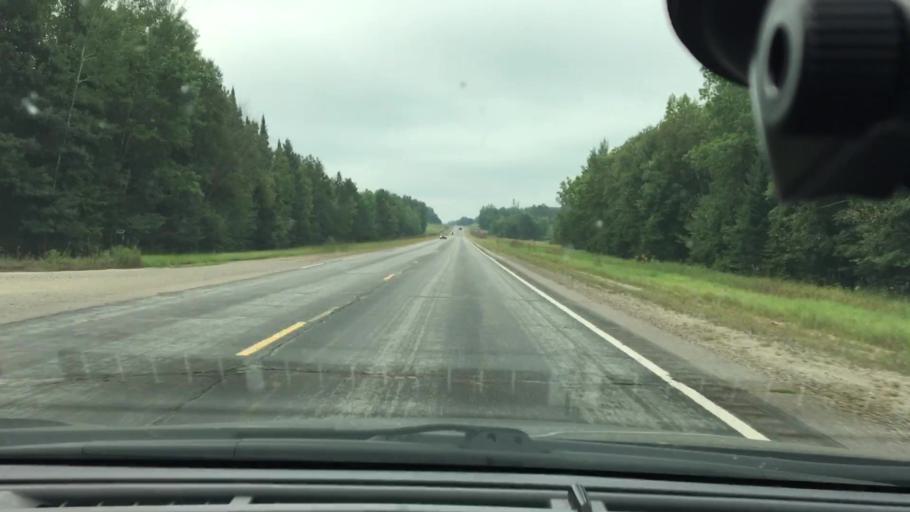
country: US
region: Minnesota
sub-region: Crow Wing County
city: Cross Lake
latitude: 46.6967
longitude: -93.9549
